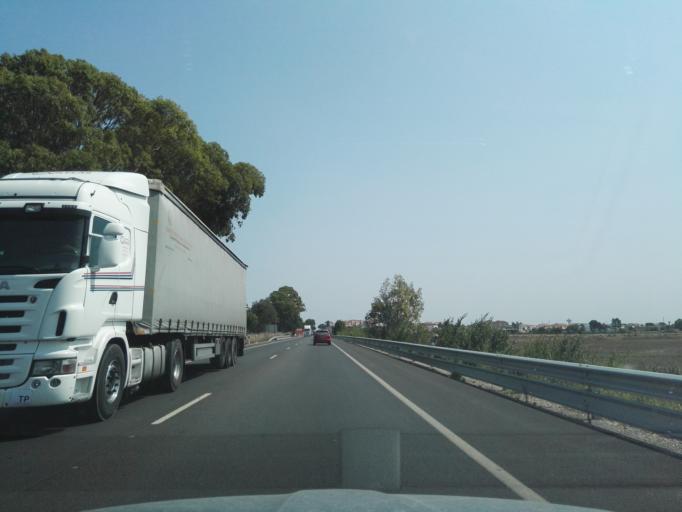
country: PT
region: Santarem
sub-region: Benavente
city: Samora Correia
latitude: 38.9268
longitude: -8.8977
